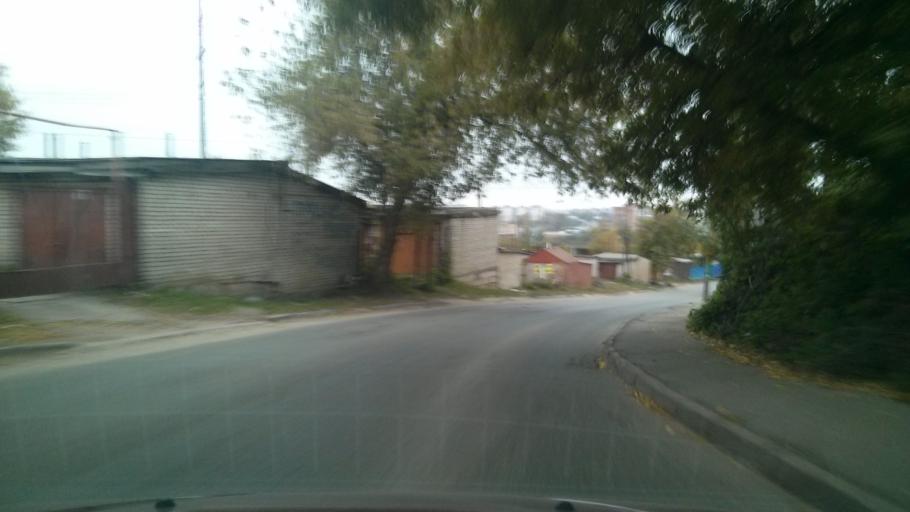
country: RU
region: Nizjnij Novgorod
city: Nizhniy Novgorod
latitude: 56.3088
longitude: 44.0090
